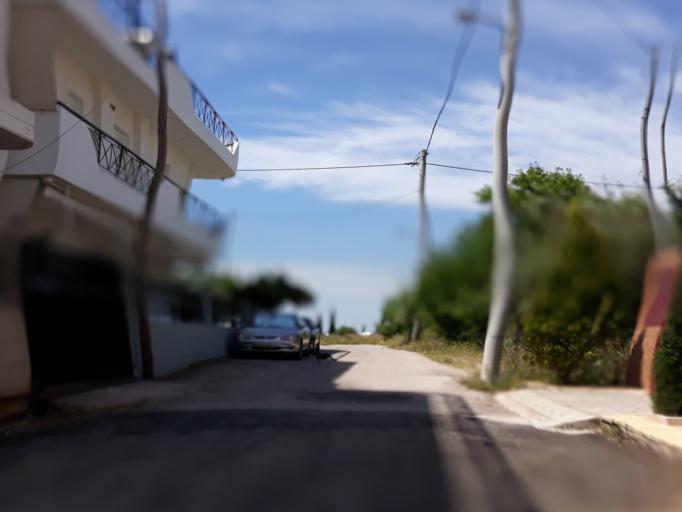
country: GR
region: Attica
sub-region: Nomarchia Dytikis Attikis
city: Ano Liosia
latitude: 38.0959
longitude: 23.6970
